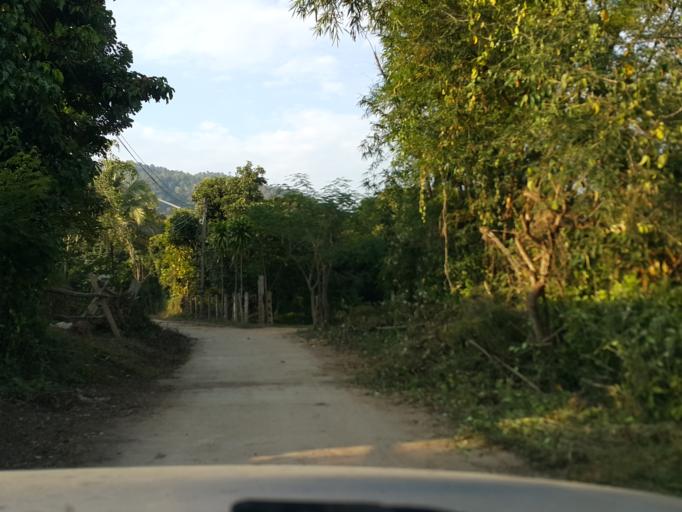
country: TH
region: Chiang Mai
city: Mae On
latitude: 18.6376
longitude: 99.2834
